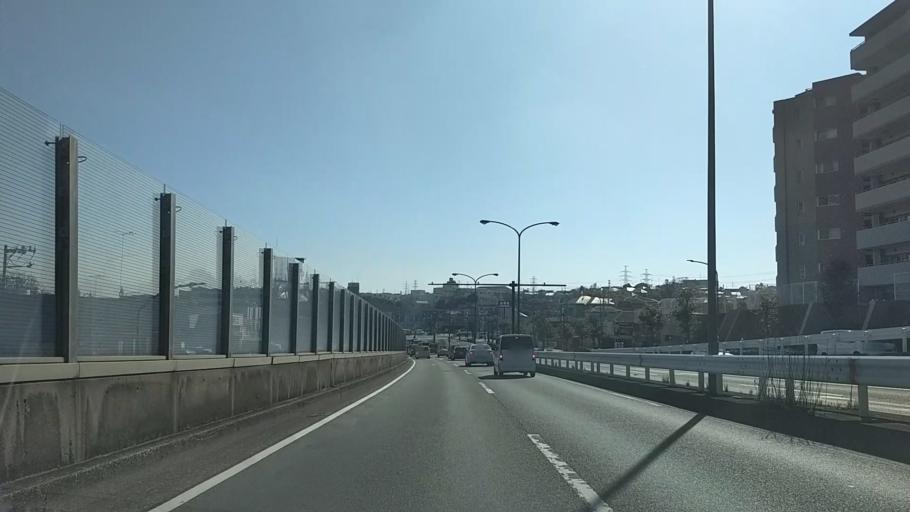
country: JP
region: Kanagawa
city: Yokohama
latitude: 35.4159
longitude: 139.5594
